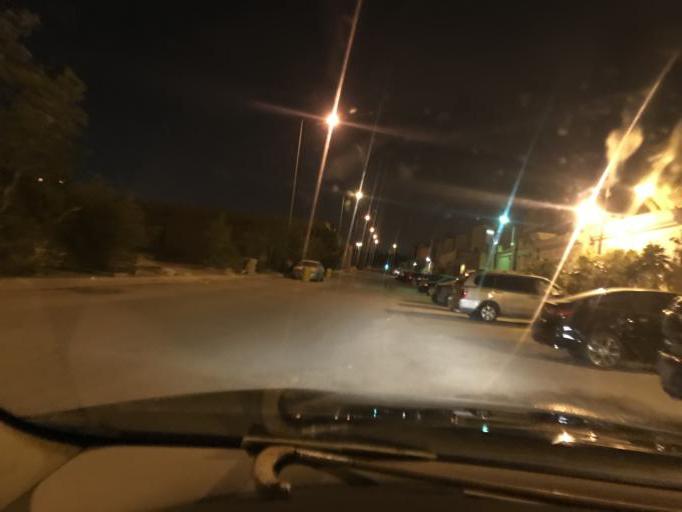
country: SA
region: Ar Riyad
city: Riyadh
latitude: 24.8170
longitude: 46.7187
